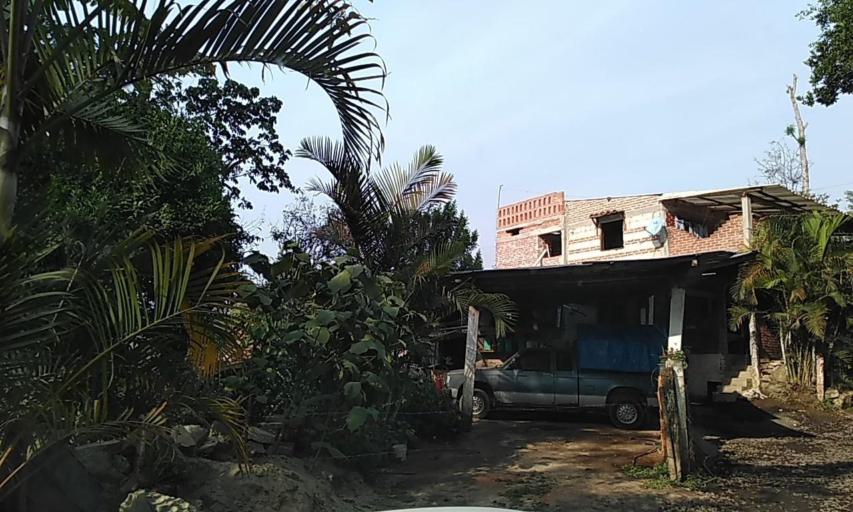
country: MX
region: Veracruz
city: El Castillo
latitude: 19.5430
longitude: -96.8473
